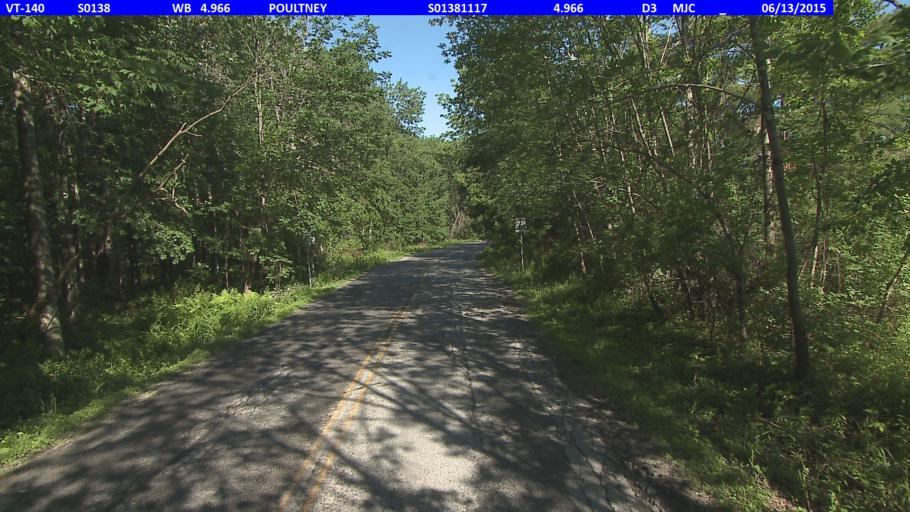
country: US
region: Vermont
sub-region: Rutland County
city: Poultney
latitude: 43.4961
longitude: -73.1706
